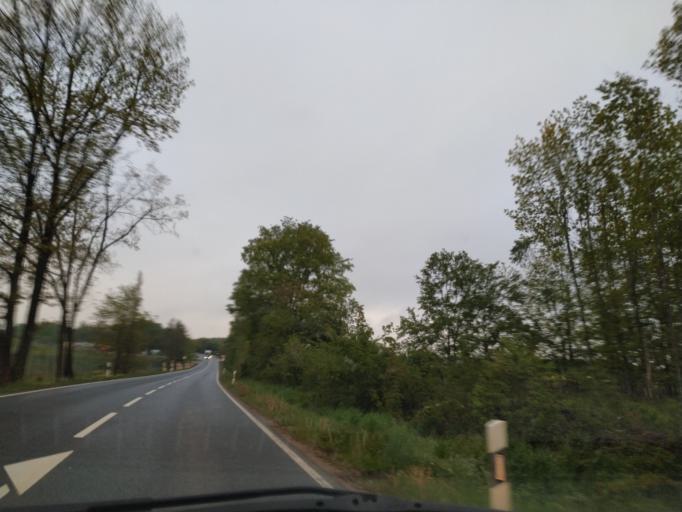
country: DE
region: Saxony
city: Hartmannsdorf
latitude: 50.7591
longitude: 12.4369
